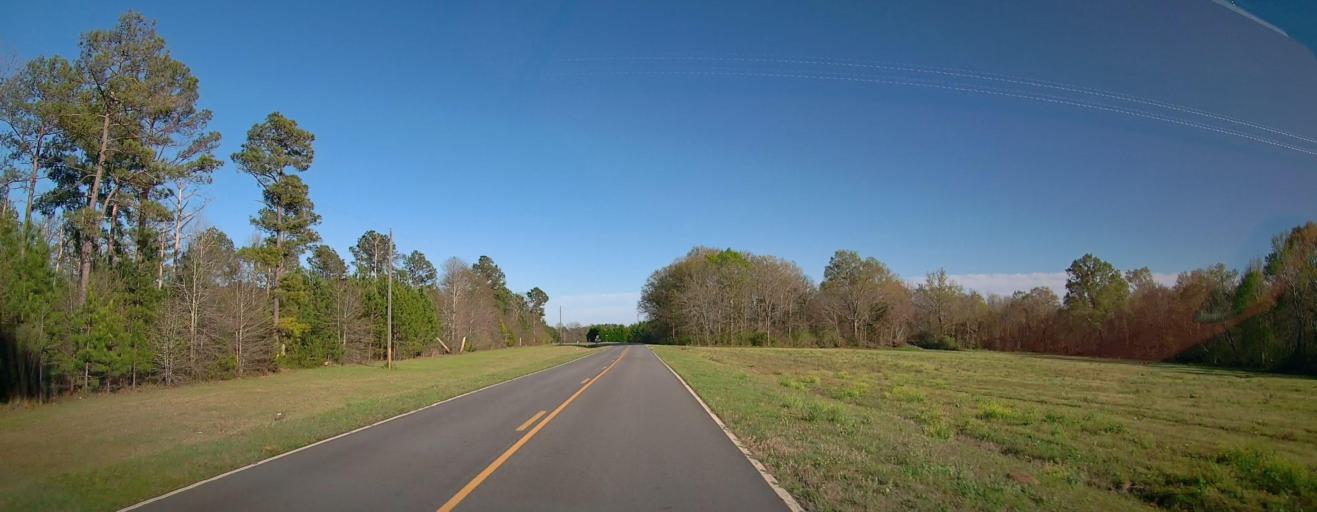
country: US
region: Georgia
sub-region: Dooly County
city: Unadilla
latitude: 32.3489
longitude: -83.6179
